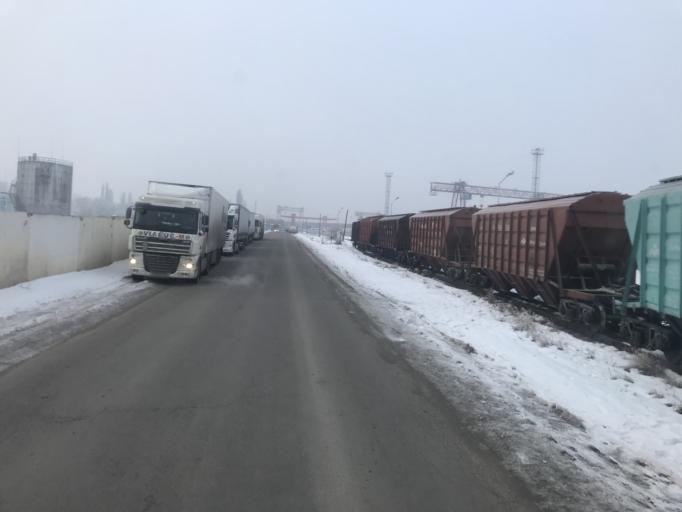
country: KZ
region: Almaty Oblysy
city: Pervomayskiy
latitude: 43.3602
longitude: 76.9765
